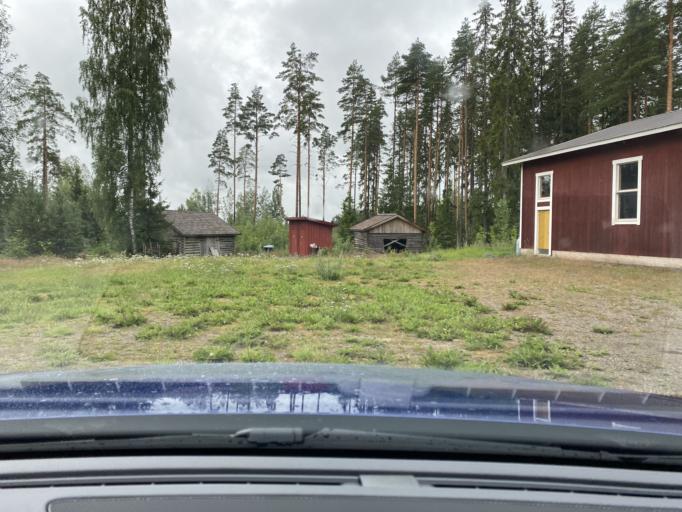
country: FI
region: Pirkanmaa
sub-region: Lounais-Pirkanmaa
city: Punkalaidun
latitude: 61.1109
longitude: 23.1347
